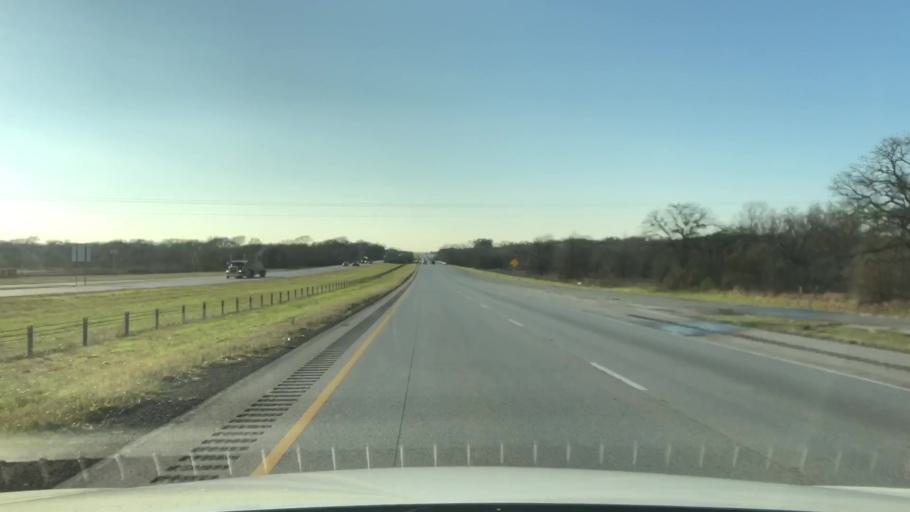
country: US
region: Texas
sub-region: Fayette County
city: Flatonia
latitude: 29.6921
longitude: -97.1801
